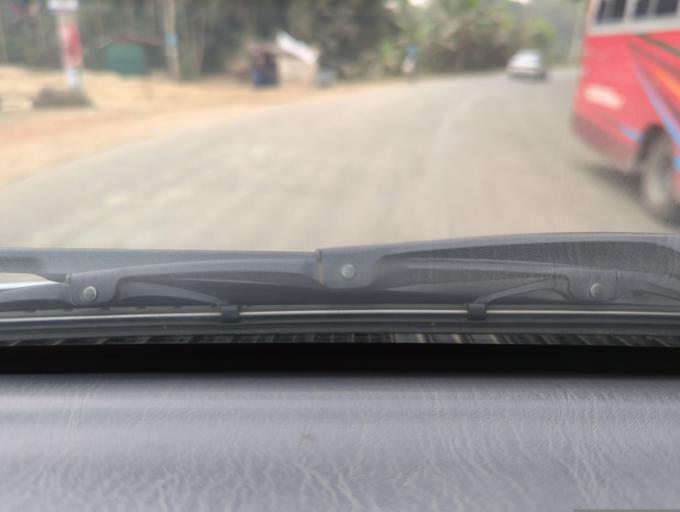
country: BD
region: Sylhet
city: Maulavi Bazar
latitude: 24.5178
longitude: 91.7300
